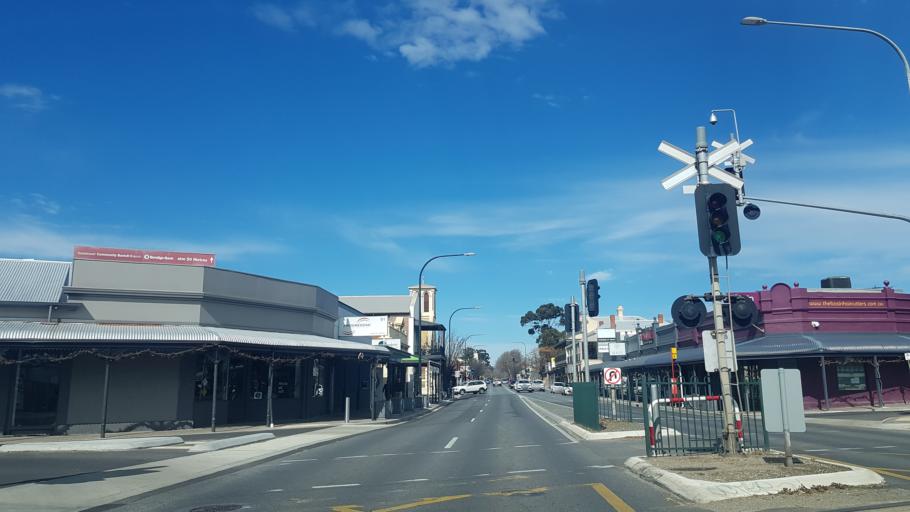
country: AU
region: South Australia
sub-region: Unley
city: Millswood
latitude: -34.9496
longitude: 138.5896
